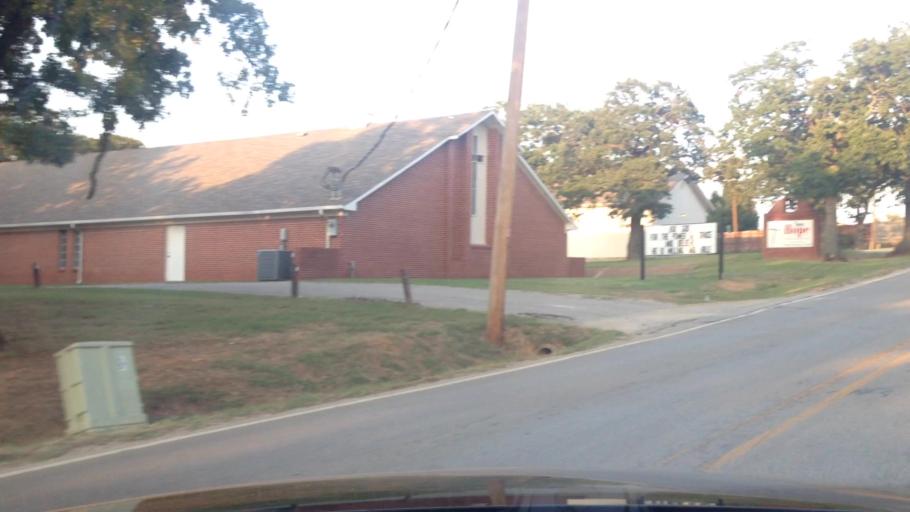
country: US
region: Texas
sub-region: Tarrant County
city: Rendon
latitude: 32.6070
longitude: -97.2153
